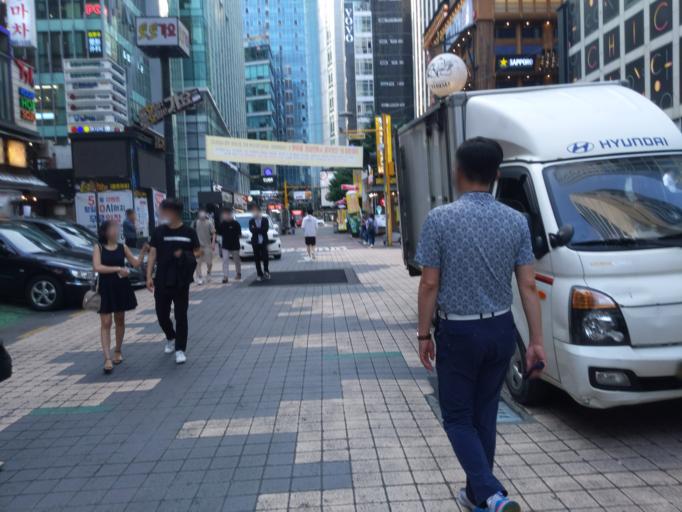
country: KR
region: Seoul
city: Seoul
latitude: 37.5015
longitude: 127.0252
